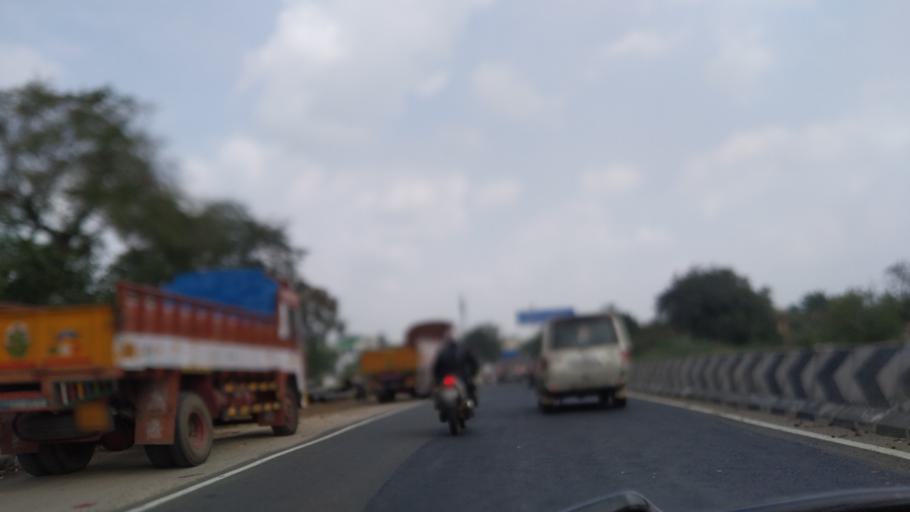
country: IN
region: Tamil Nadu
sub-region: Coimbatore
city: Madukkarai
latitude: 10.9285
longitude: 76.9495
